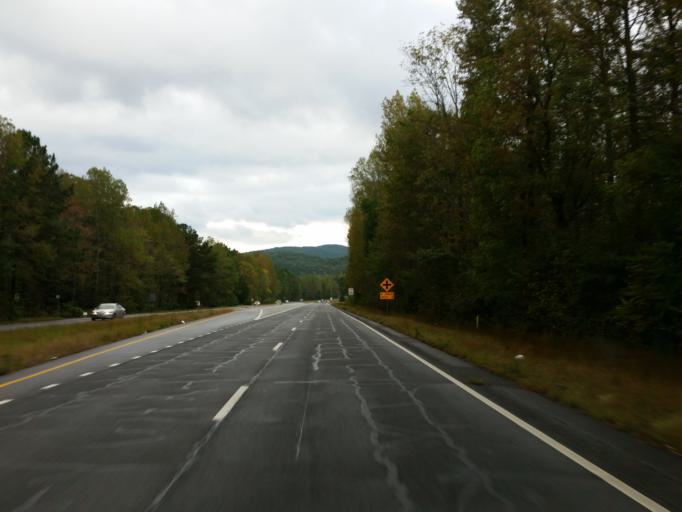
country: US
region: Georgia
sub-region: Bartow County
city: Emerson
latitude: 34.1028
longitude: -84.7452
